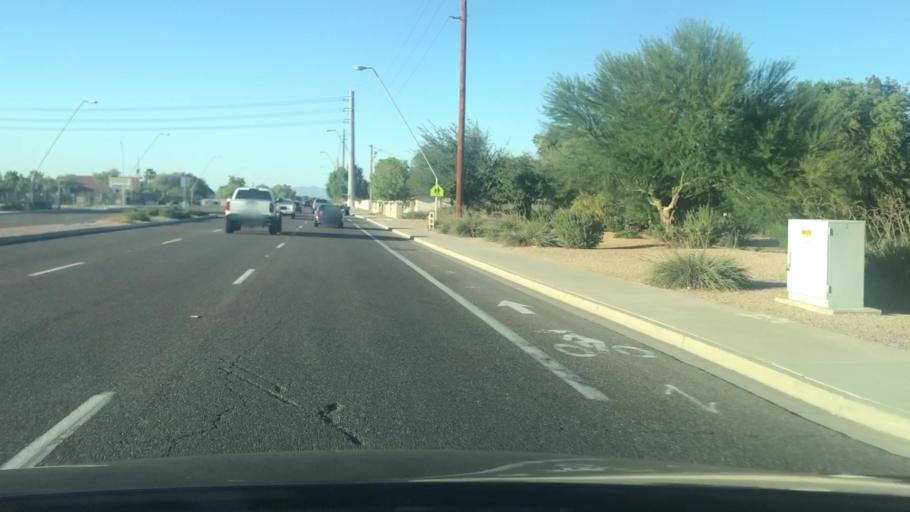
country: US
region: Arizona
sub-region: Maricopa County
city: Chandler
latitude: 33.2978
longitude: -111.8069
